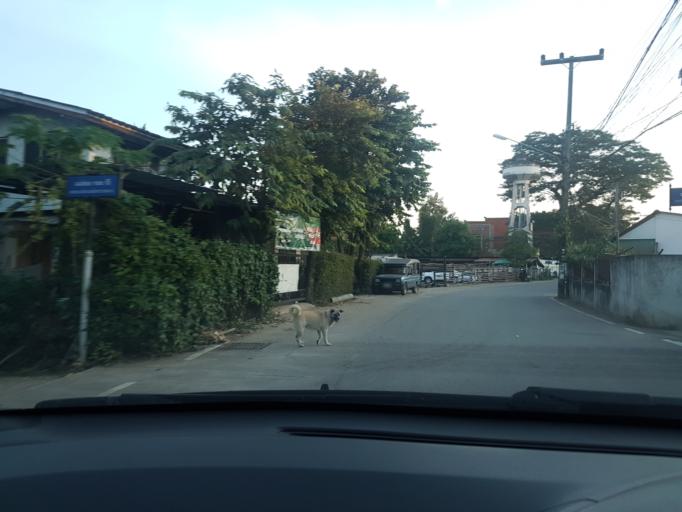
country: TH
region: Chiang Mai
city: San Sai
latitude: 18.8337
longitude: 99.0447
